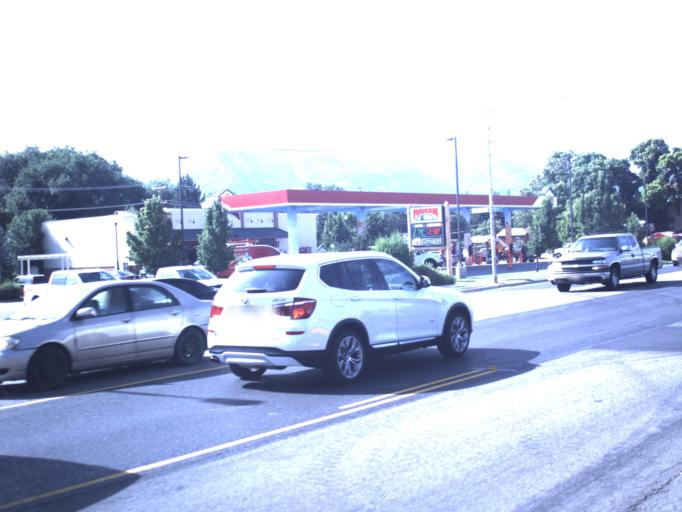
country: US
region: Utah
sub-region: Wasatch County
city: Heber
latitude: 40.5127
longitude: -111.4133
